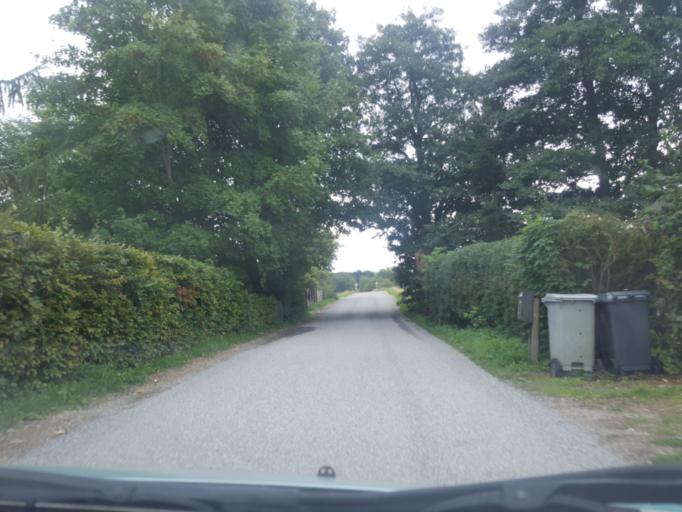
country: DK
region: Zealand
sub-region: Soro Kommune
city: Soro
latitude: 55.4553
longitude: 11.5197
